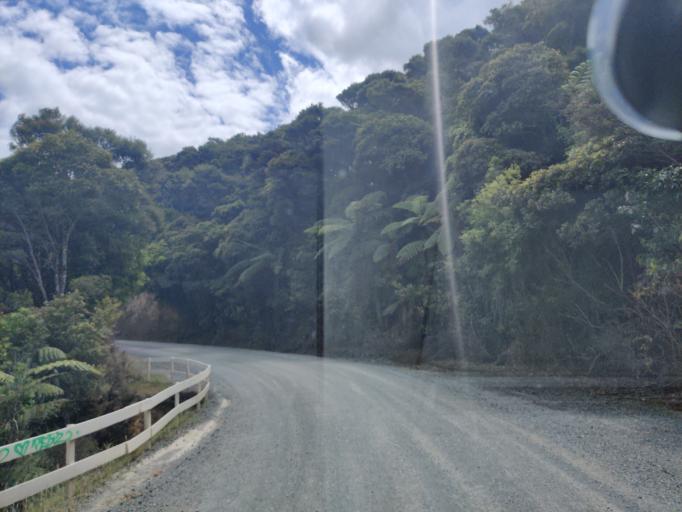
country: NZ
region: Northland
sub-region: Far North District
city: Paihia
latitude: -35.2610
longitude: 174.0478
